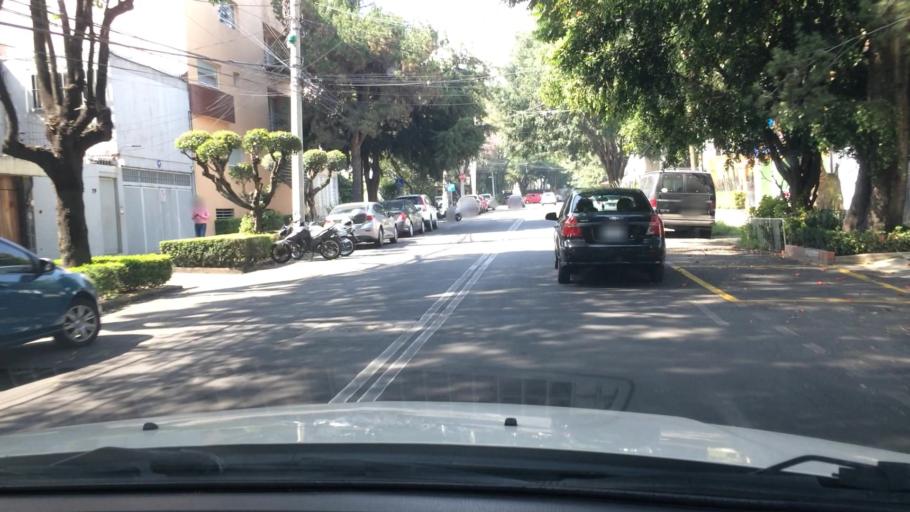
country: MX
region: Mexico City
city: Alvaro Obregon
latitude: 19.3634
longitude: -99.1839
